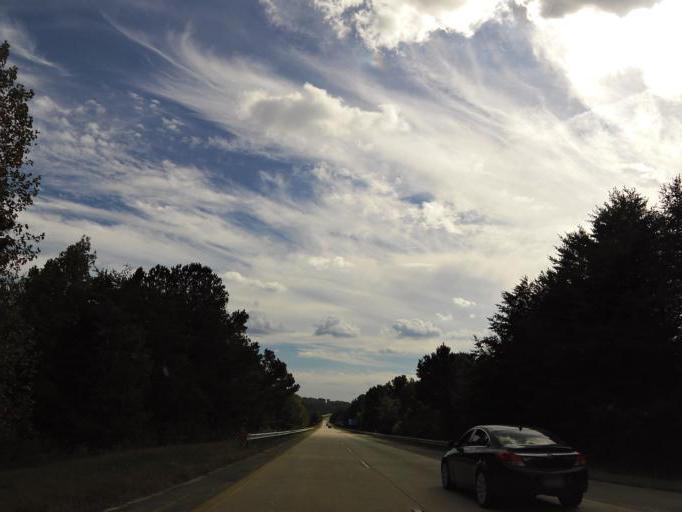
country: US
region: Georgia
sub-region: Cherokee County
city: Ball Ground
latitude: 34.3512
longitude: -84.3917
